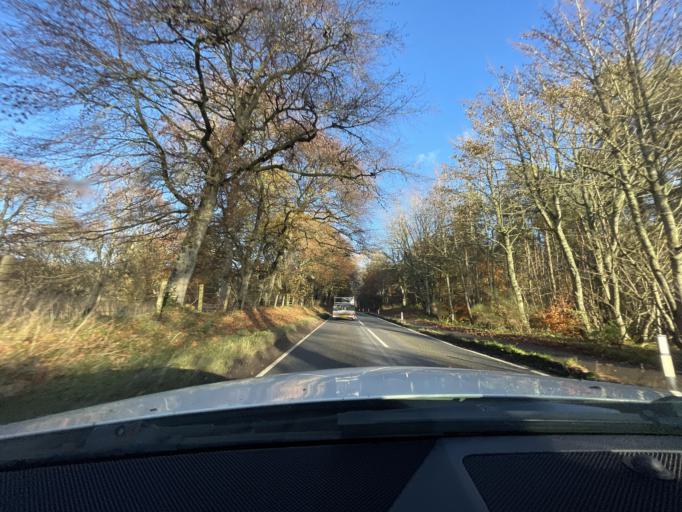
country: GB
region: Scotland
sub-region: Highland
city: Inverness
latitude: 57.4332
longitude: -4.2744
